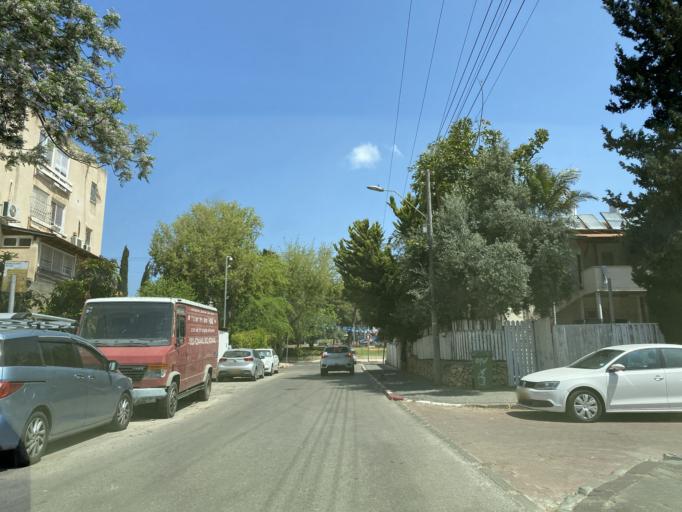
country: IL
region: Tel Aviv
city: Ramat HaSharon
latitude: 32.1560
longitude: 34.8366
